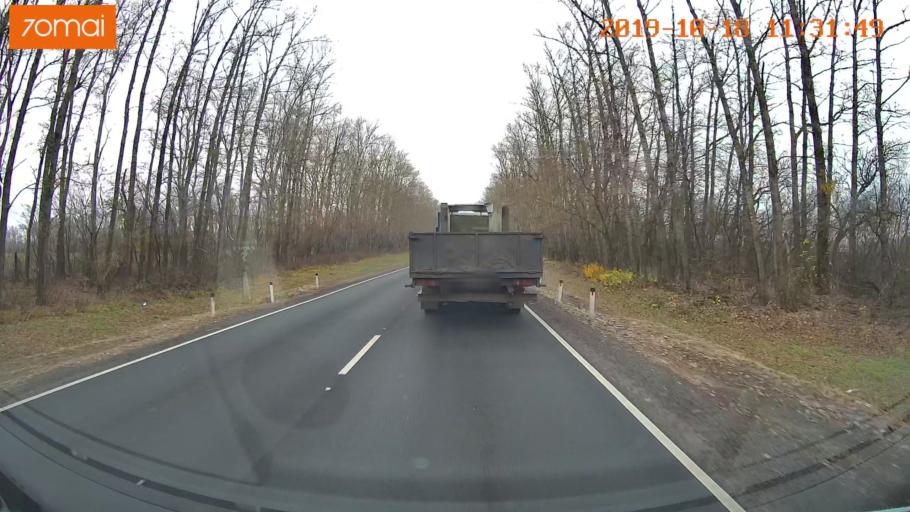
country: RU
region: Rjazan
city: Oktyabr'skiy
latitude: 54.1422
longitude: 38.7023
